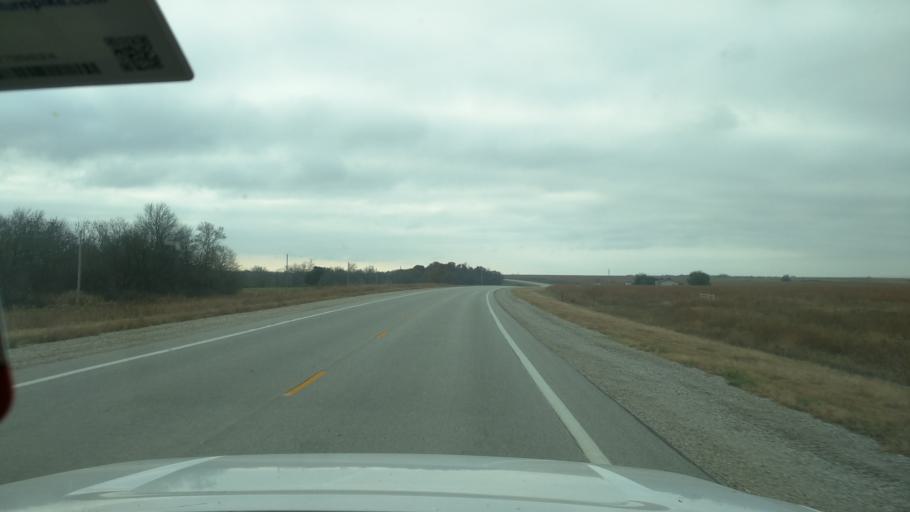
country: US
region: Kansas
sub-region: Elk County
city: Howard
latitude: 37.5442
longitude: -96.2534
